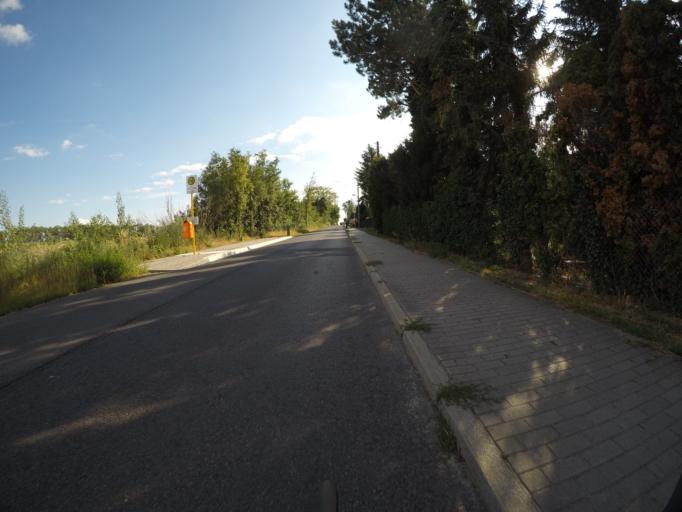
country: DE
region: Berlin
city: Falkenberg
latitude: 52.5867
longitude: 13.5365
